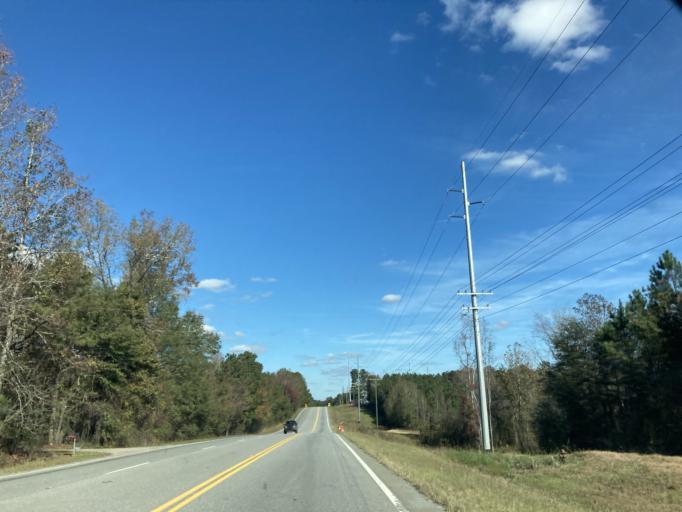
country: US
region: Georgia
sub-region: Jones County
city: Gray
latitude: 32.9257
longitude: -83.5071
